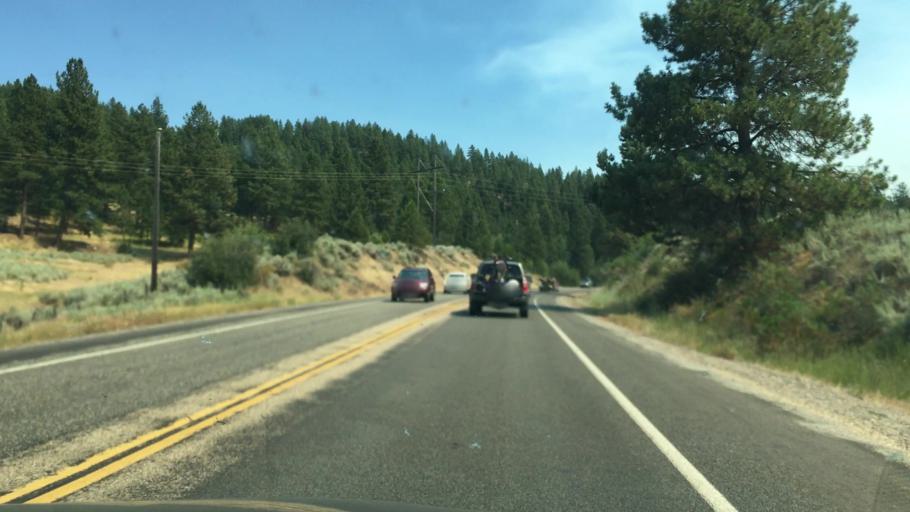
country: US
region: Idaho
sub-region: Valley County
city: Cascade
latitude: 44.5959
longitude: -116.0435
